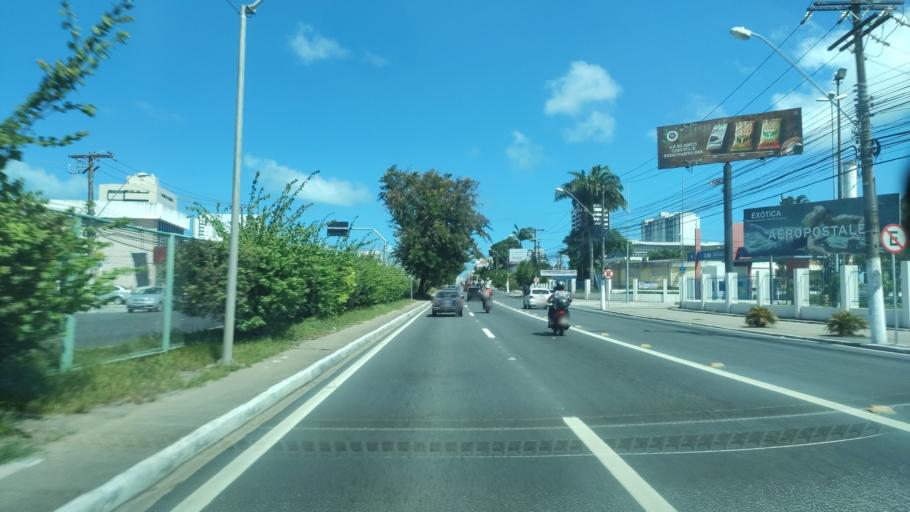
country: BR
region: Alagoas
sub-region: Maceio
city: Maceio
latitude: -9.6389
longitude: -35.7357
